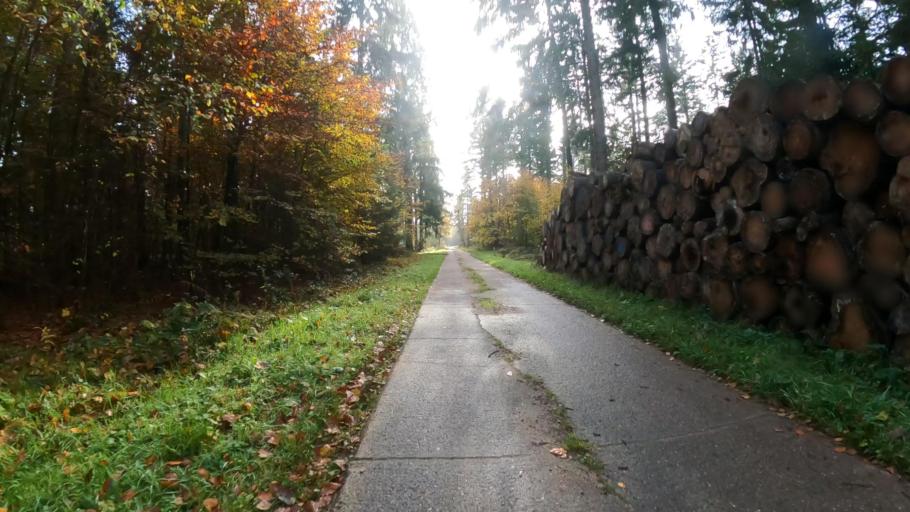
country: DE
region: Lower Saxony
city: Buchholz in der Nordheide
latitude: 53.3463
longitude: 9.8206
